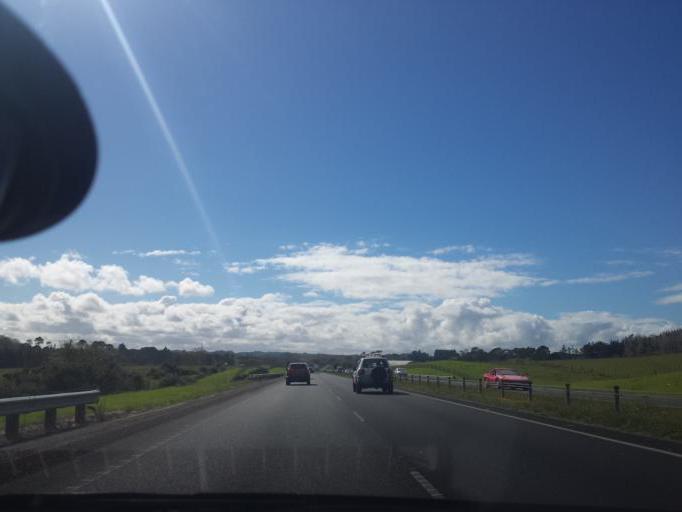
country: NZ
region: Auckland
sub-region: Auckland
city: Rothesay Bay
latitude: -36.6396
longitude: 174.6626
